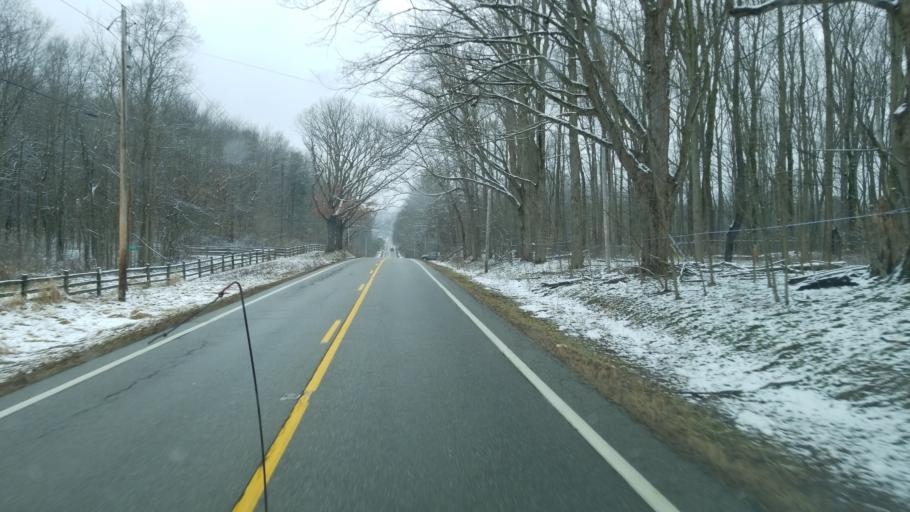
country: US
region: Ohio
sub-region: Portage County
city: Hiram
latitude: 41.3097
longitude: -81.1189
